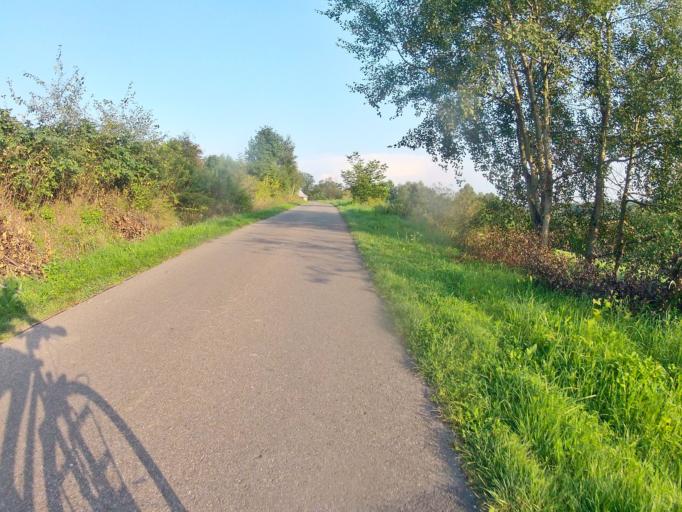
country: PL
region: Subcarpathian Voivodeship
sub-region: Powiat jasielski
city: Brzyska
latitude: 49.7899
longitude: 21.3702
